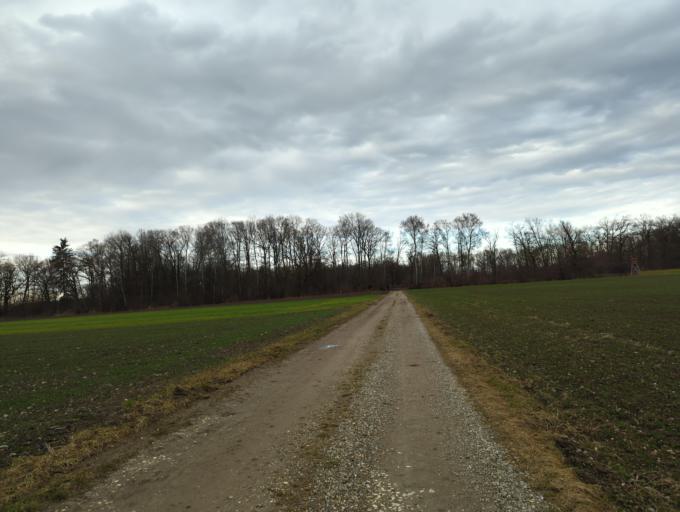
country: DE
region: Bavaria
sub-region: Swabia
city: Guenzburg
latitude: 48.4773
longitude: 10.3056
